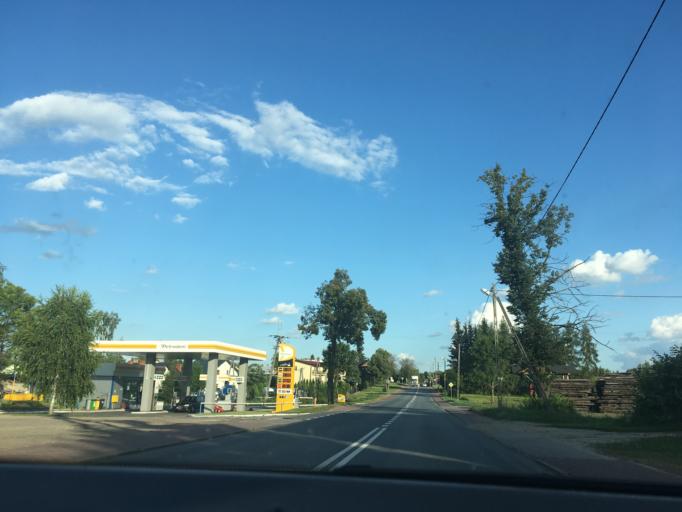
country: PL
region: Masovian Voivodeship
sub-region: Powiat losicki
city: Sarnaki
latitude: 52.3200
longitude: 22.8830
